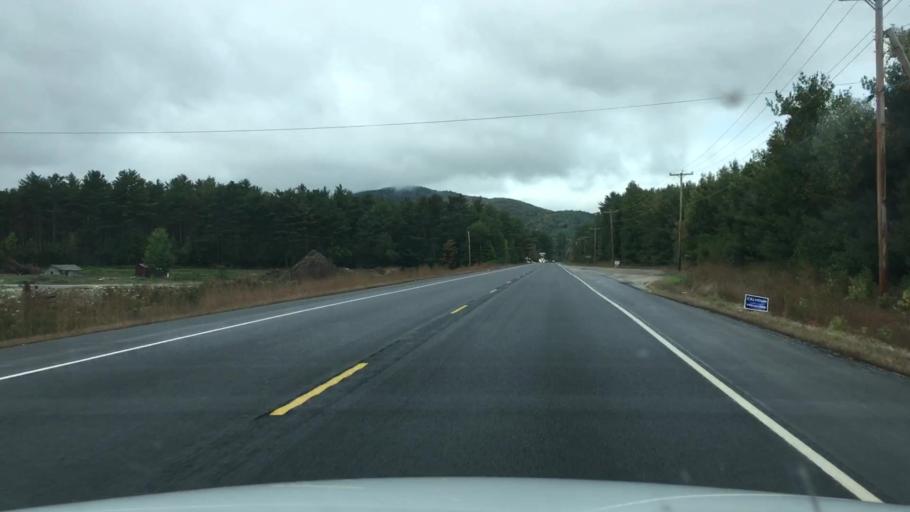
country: US
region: Maine
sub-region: Oxford County
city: Bethel
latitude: 44.4114
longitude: -70.8472
